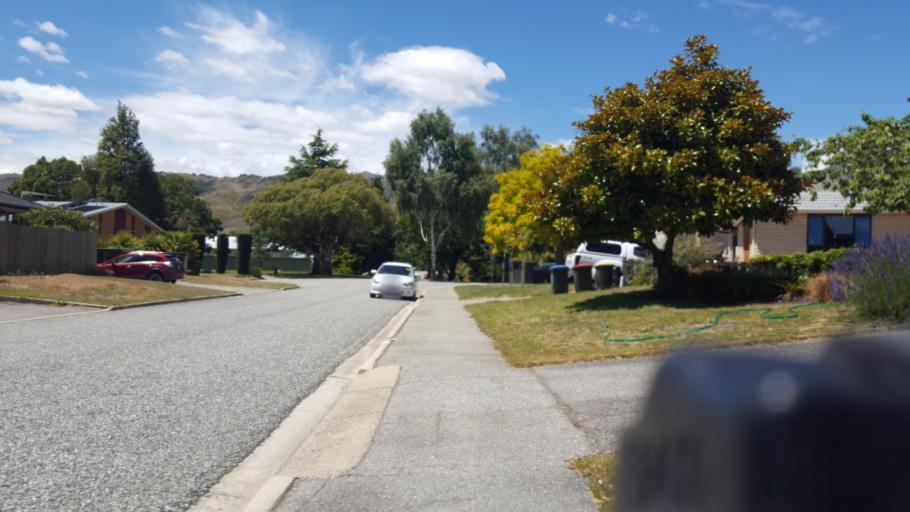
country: NZ
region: Otago
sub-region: Queenstown-Lakes District
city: Wanaka
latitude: -45.0413
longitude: 169.2030
